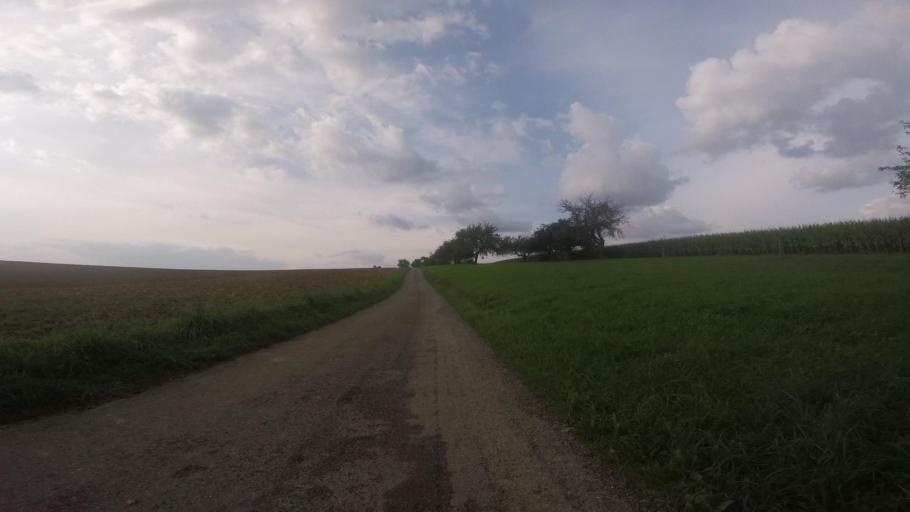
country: DE
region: Baden-Wuerttemberg
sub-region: Regierungsbezirk Stuttgart
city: Aspach
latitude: 48.9598
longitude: 9.3865
